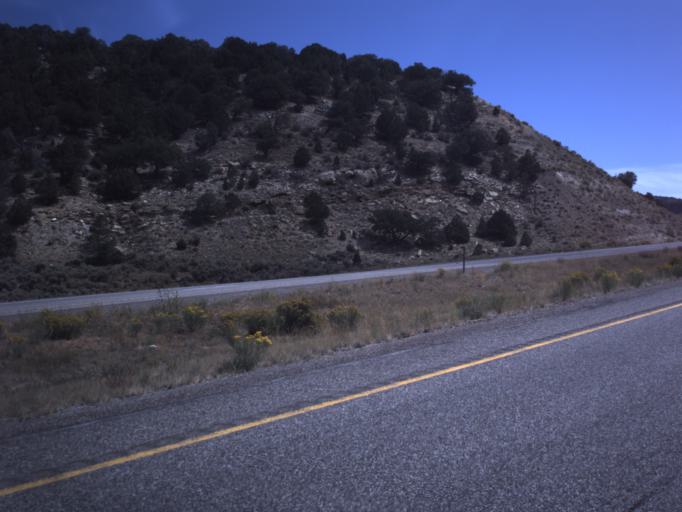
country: US
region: Utah
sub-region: Sevier County
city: Salina
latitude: 38.8066
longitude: -111.5304
